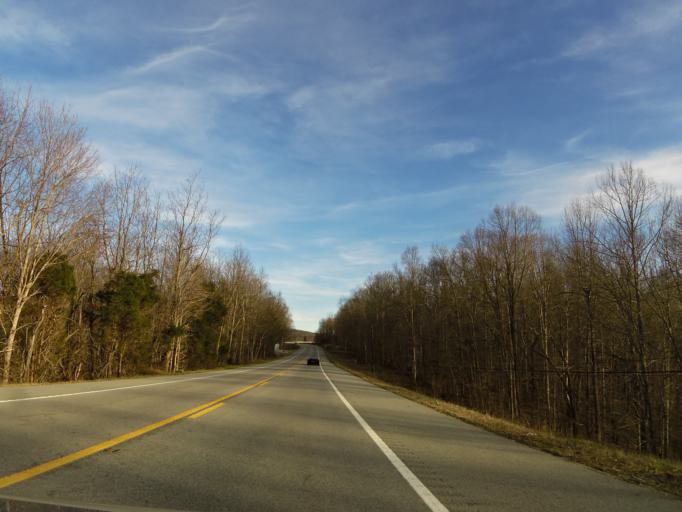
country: US
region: Tennessee
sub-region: White County
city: Sparta
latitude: 35.9254
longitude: -85.4163
